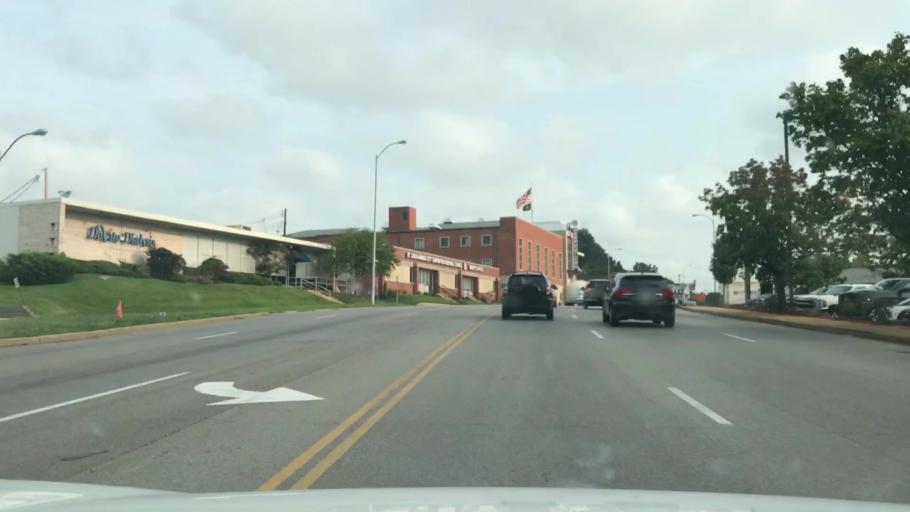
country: US
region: Missouri
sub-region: Saint Louis County
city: Richmond Heights
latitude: 38.6242
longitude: -90.2878
